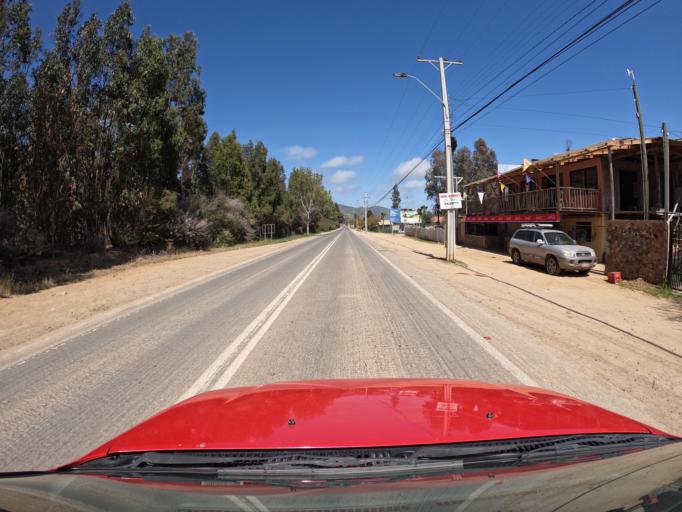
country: CL
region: O'Higgins
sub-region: Provincia de Colchagua
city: Santa Cruz
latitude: -34.7195
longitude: -71.6355
